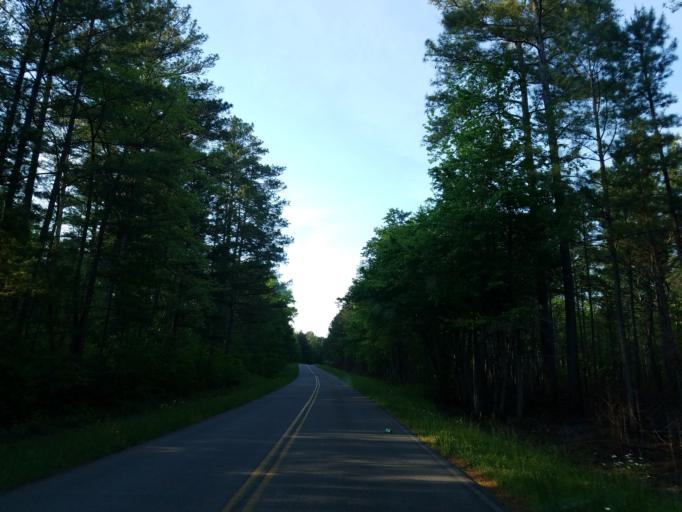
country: US
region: Georgia
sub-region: Gordon County
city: Calhoun
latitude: 34.6032
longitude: -85.0816
